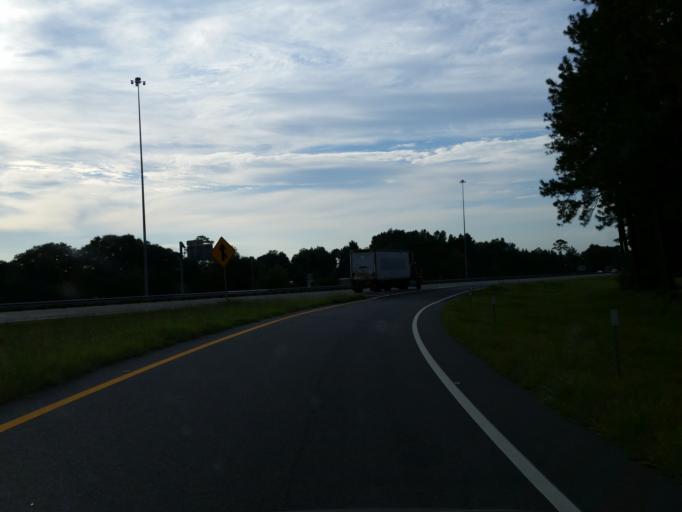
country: US
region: Georgia
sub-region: Echols County
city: Statenville
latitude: 30.5966
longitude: -83.1214
